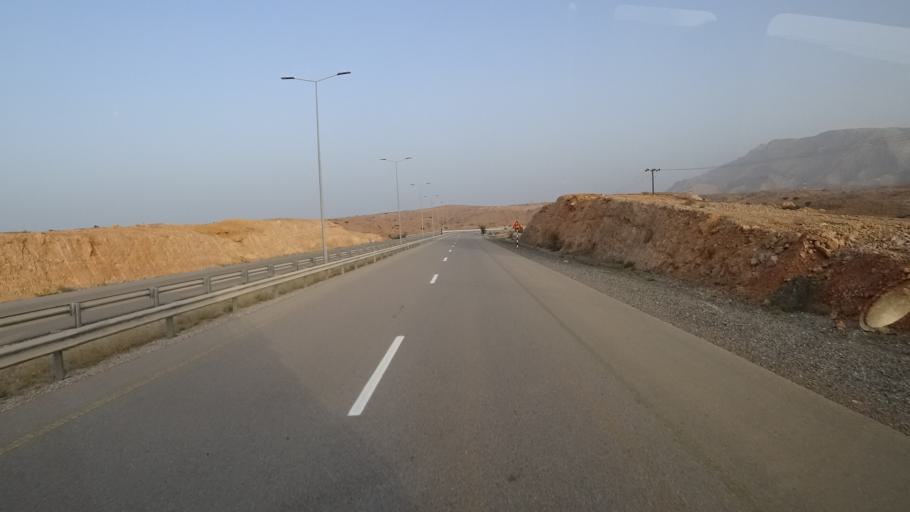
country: OM
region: Ash Sharqiyah
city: Al Qabil
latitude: 23.1000
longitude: 58.9945
